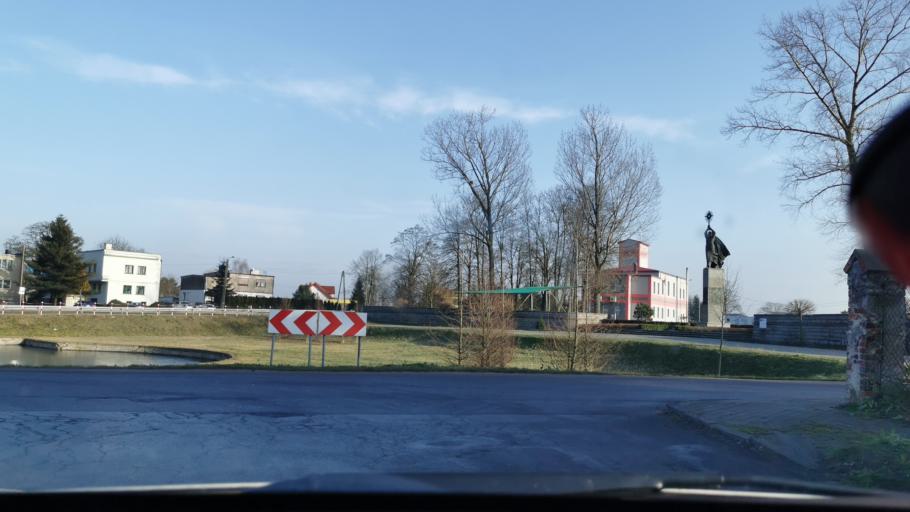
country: PL
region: Lodz Voivodeship
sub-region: Powiat sieradzki
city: Blaszki
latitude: 51.6850
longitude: 18.3286
